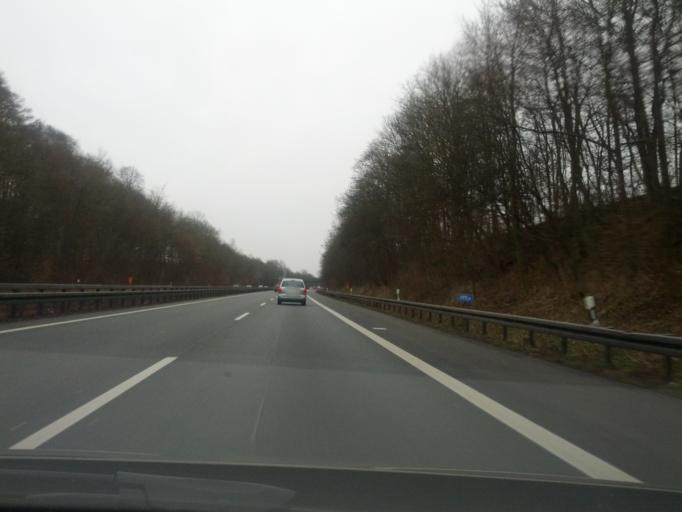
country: DE
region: Lower Saxony
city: Holle
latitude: 52.0958
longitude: 10.1631
